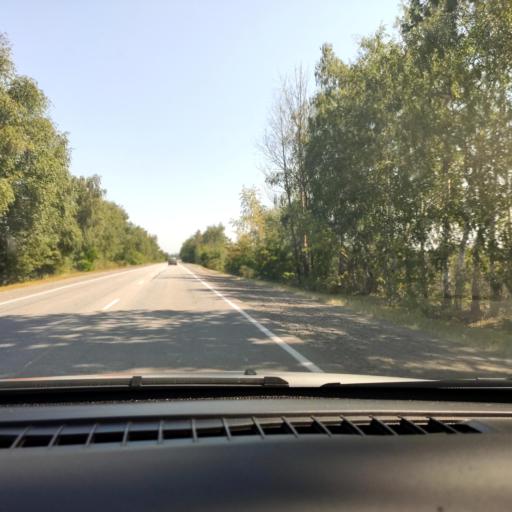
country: RU
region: Voronezj
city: Ostrogozhsk
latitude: 50.8258
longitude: 39.1663
